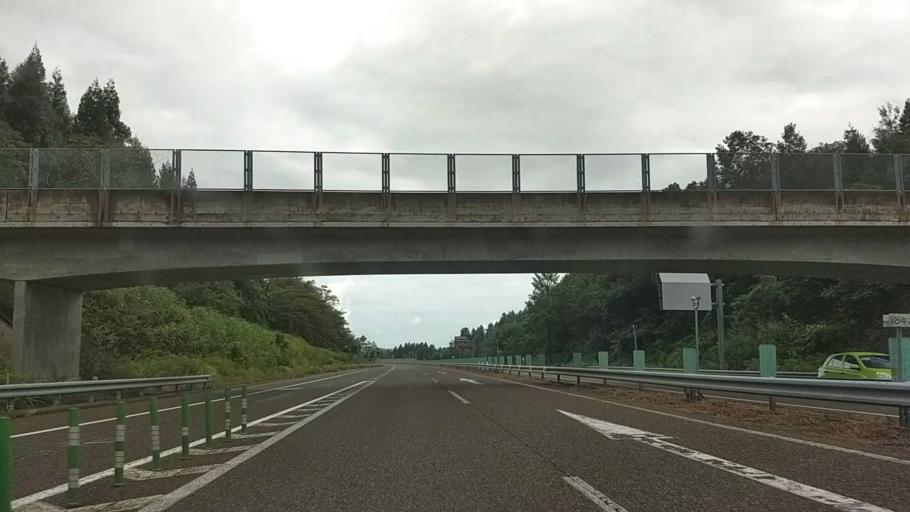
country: JP
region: Niigata
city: Arai
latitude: 36.9713
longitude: 138.2213
